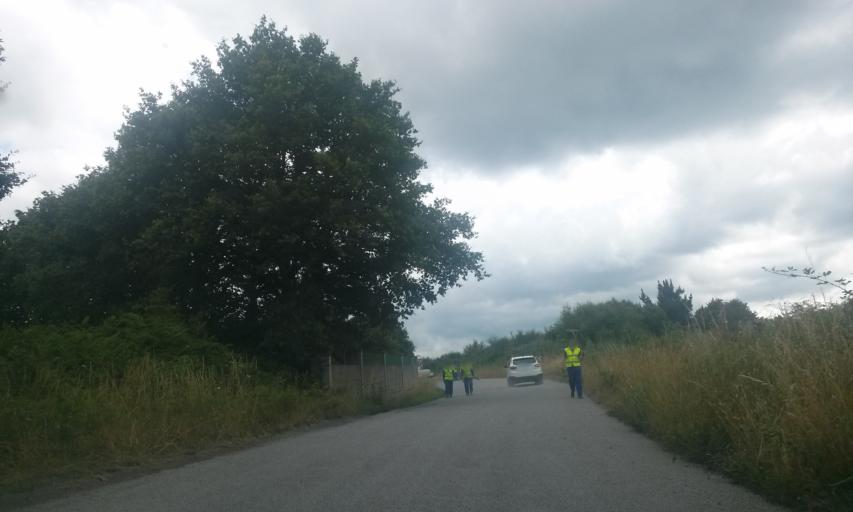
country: ES
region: Galicia
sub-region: Provincia de Lugo
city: Outeiro de Rei
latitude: 43.0644
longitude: -7.6160
